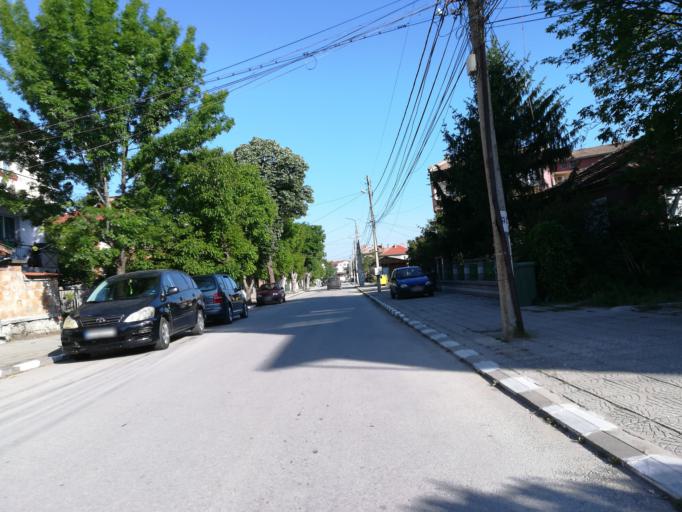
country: BG
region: Stara Zagora
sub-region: Obshtina Chirpan
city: Chirpan
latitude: 42.1025
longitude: 25.2230
